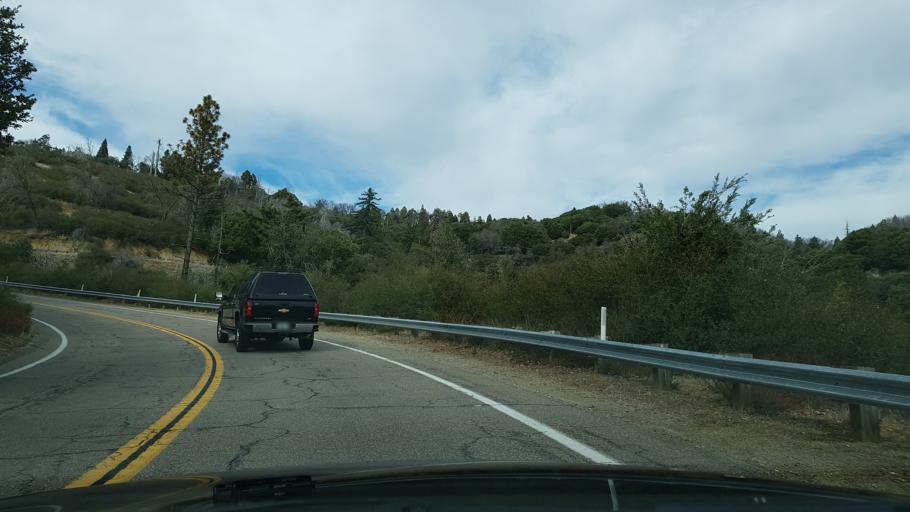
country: US
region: California
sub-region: Riverside County
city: Aguanga
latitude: 33.3110
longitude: -116.8706
